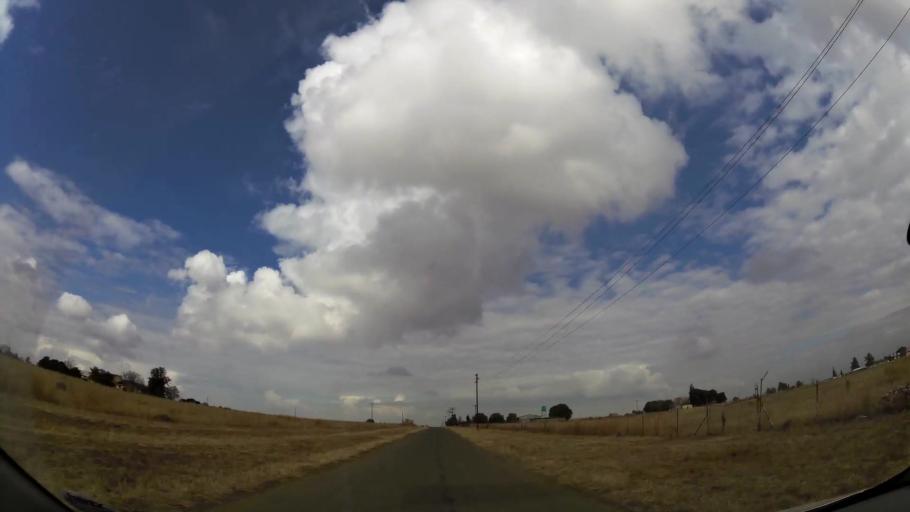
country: ZA
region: Gauteng
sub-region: Sedibeng District Municipality
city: Meyerton
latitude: -26.6096
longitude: 28.0768
